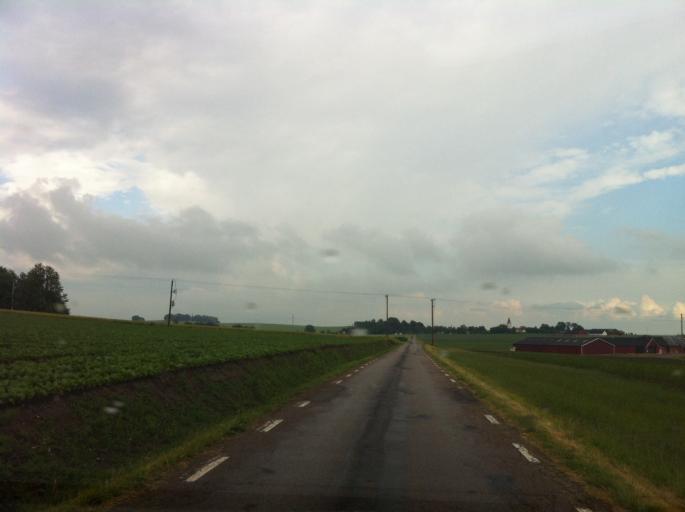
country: SE
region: Skane
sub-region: Helsingborg
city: Glumslov
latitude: 55.9214
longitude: 12.8699
